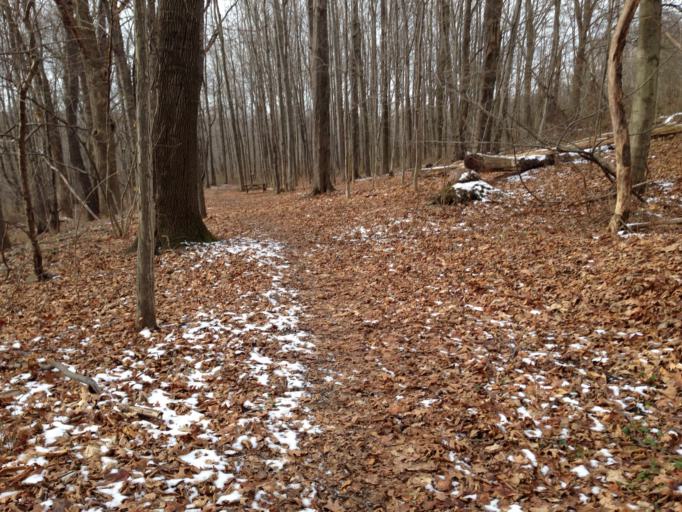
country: US
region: New York
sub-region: Tompkins County
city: East Ithaca
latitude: 42.4194
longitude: -76.4488
